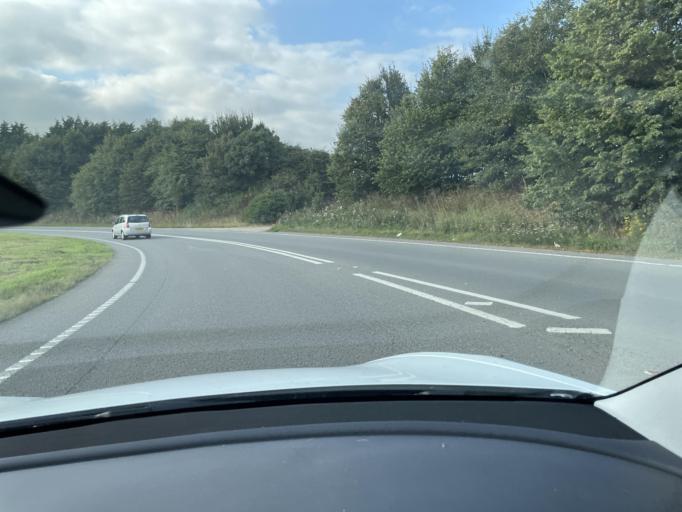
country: GB
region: England
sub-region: Northamptonshire
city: Long Buckby
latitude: 52.3978
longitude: -1.0304
